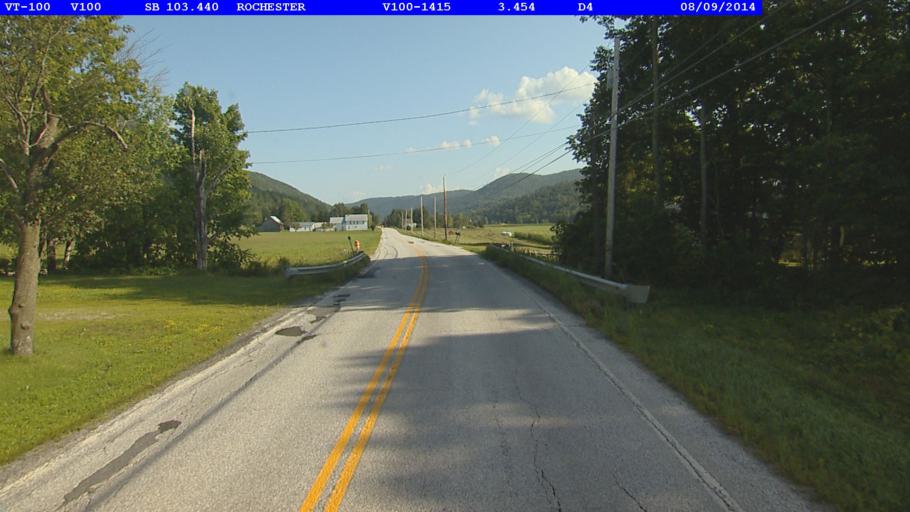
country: US
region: Vermont
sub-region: Orange County
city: Randolph
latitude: 43.8513
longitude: -72.8010
